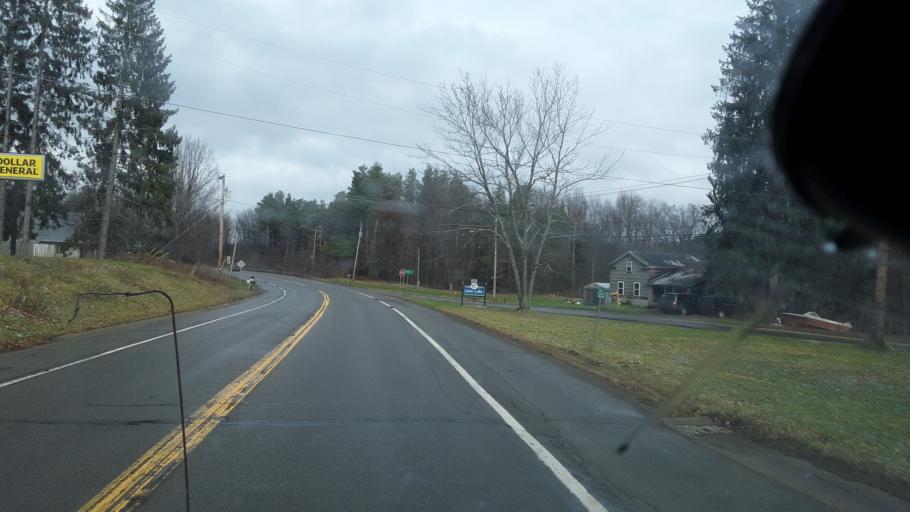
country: US
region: New York
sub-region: Cattaraugus County
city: Delevan
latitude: 42.4352
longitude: -78.4794
